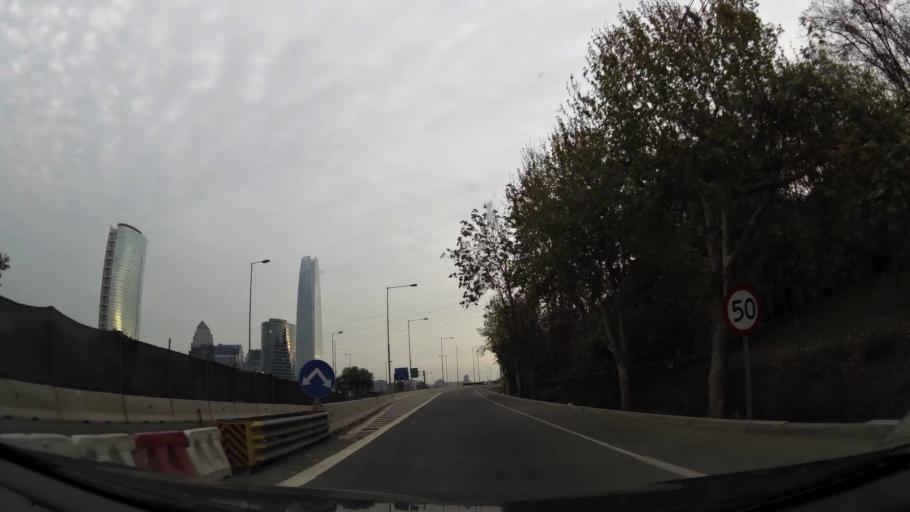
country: CL
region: Santiago Metropolitan
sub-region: Provincia de Santiago
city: Villa Presidente Frei, Nunoa, Santiago, Chile
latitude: -33.4085
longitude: -70.6060
